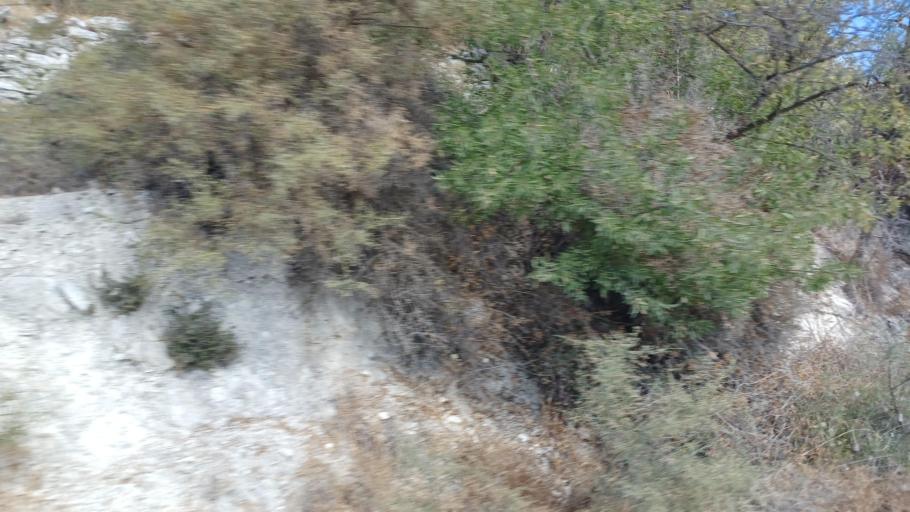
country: CY
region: Limassol
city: Pachna
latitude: 34.8163
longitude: 32.6776
